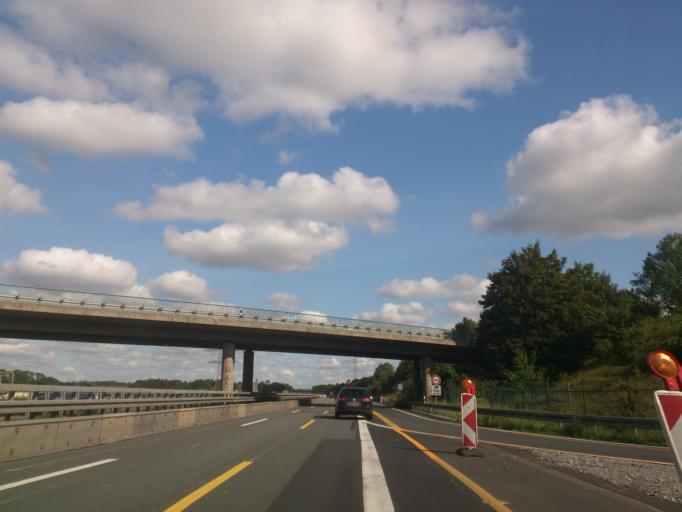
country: DE
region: North Rhine-Westphalia
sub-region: Regierungsbezirk Detmold
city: Hovelhof
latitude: 51.8566
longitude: 8.6673
